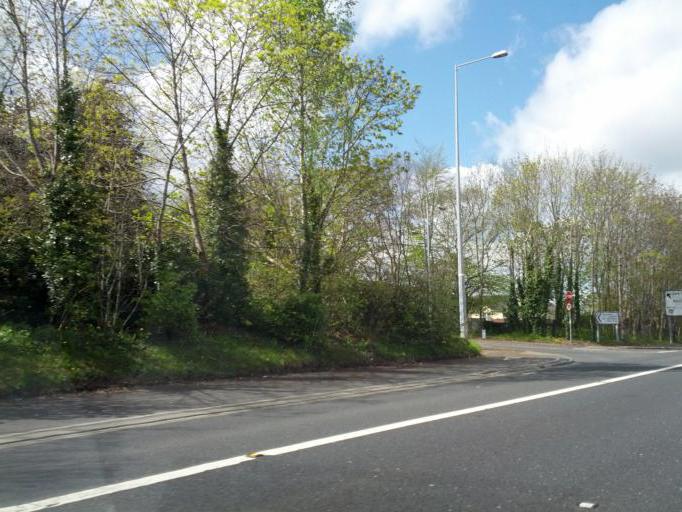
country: IE
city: Palmerstown
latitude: 53.3580
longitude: -6.4076
